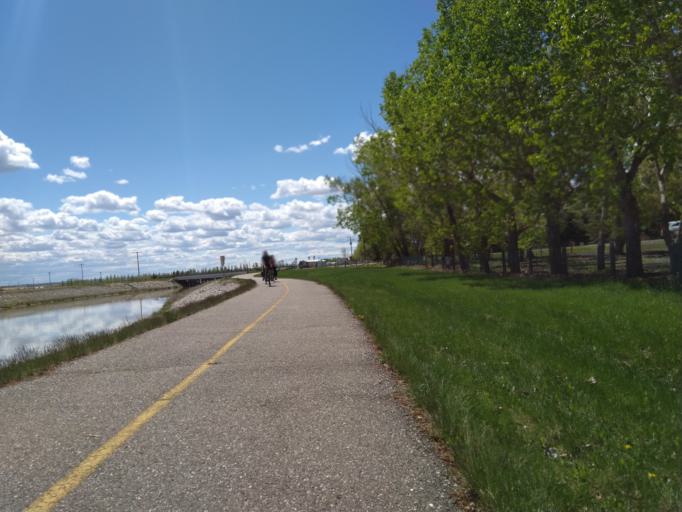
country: CA
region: Alberta
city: Chestermere
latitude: 50.9903
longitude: -113.8644
